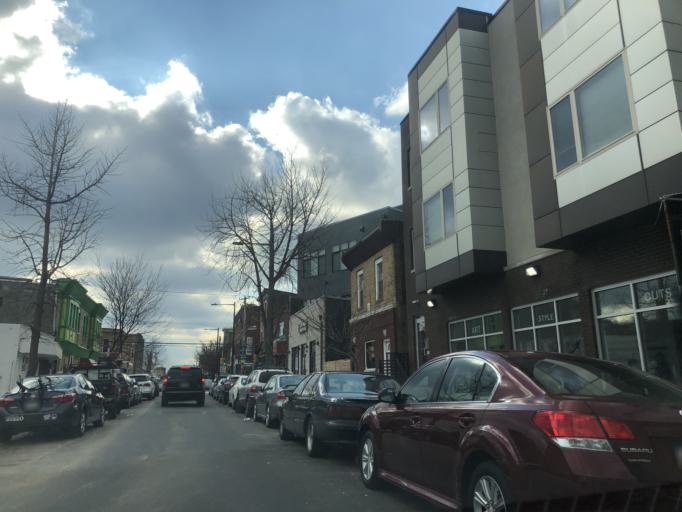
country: US
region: Pennsylvania
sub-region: Philadelphia County
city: Philadelphia
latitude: 39.9360
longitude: -75.1780
